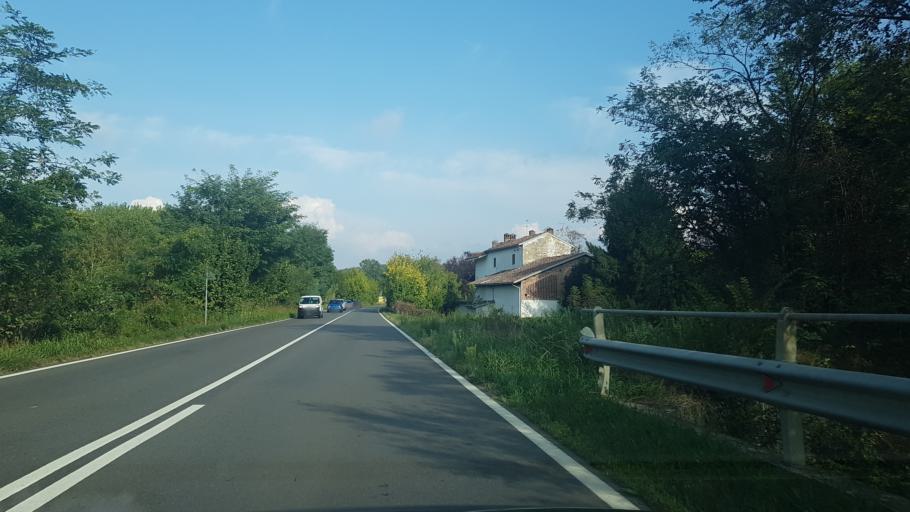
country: IT
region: Piedmont
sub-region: Provincia di Asti
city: Bruno
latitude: 44.7976
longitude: 8.4330
